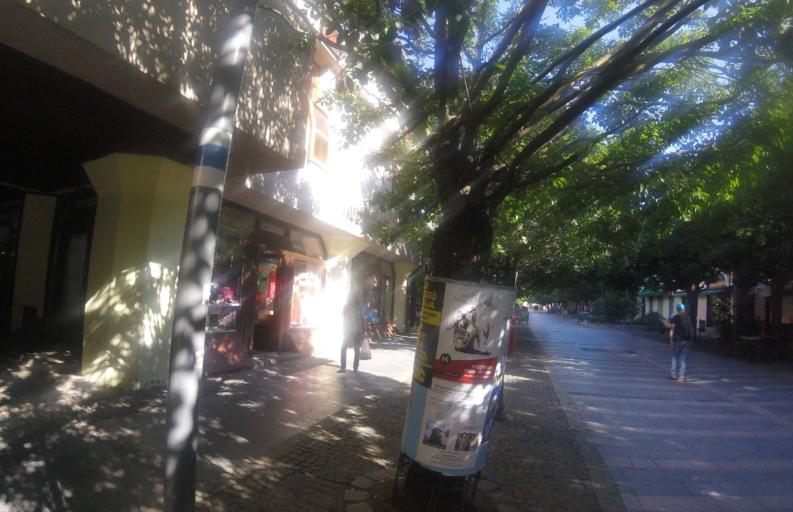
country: HU
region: Zala
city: Keszthely
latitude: 46.7673
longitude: 17.2426
